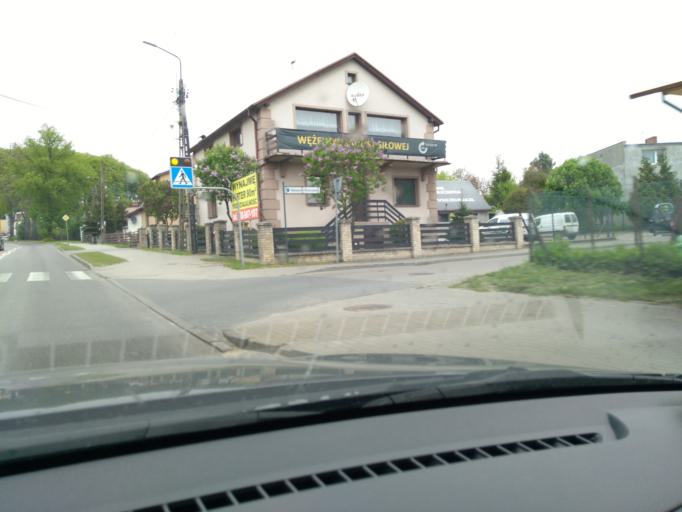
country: PL
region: Pomeranian Voivodeship
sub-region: Powiat kartuski
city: Kartuzy
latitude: 54.3369
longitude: 18.1881
